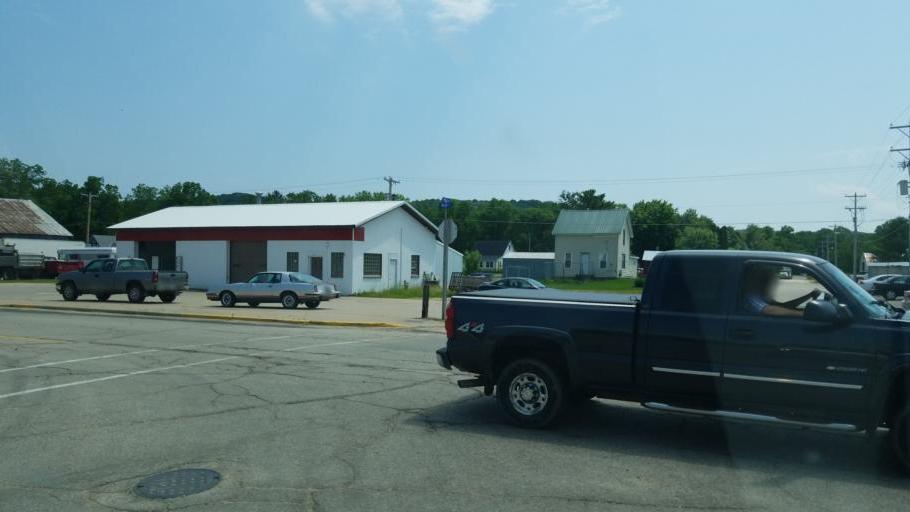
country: US
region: Wisconsin
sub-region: Monroe County
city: Cashton
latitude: 43.5745
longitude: -90.6414
